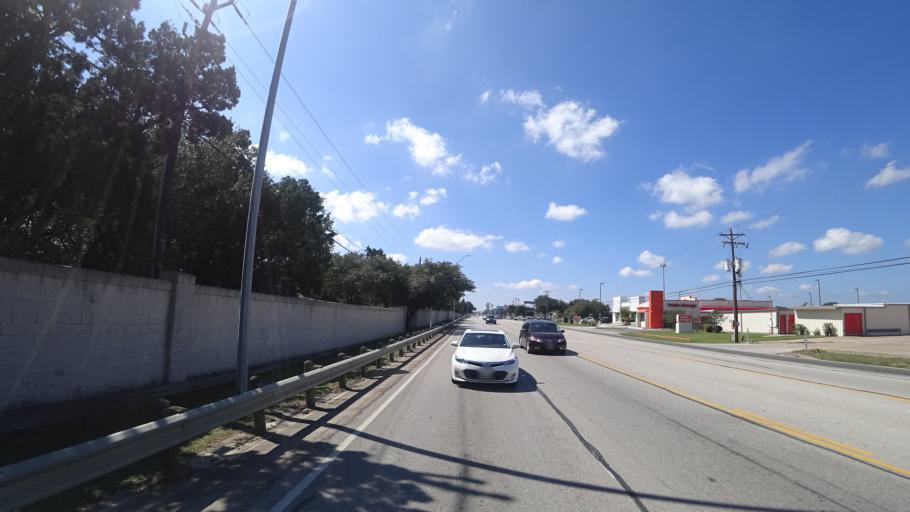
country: US
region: Texas
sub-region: Williamson County
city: Anderson Mill
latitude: 30.4637
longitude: -97.8111
